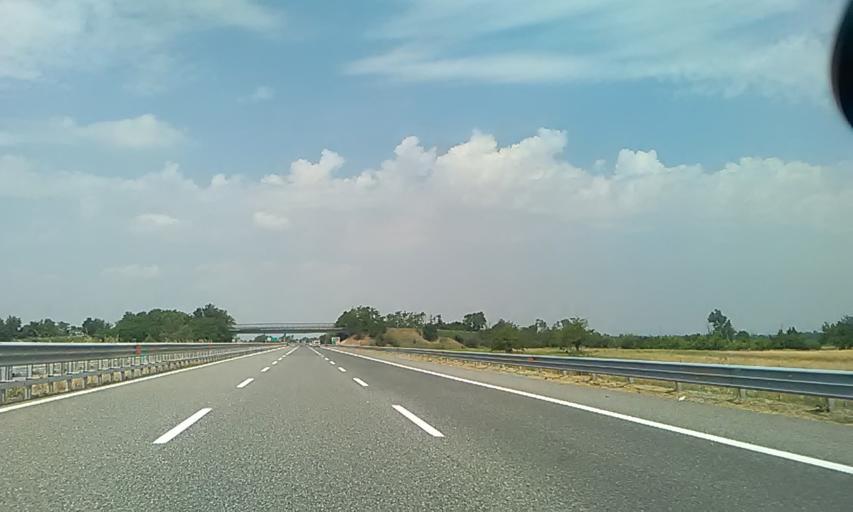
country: IT
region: Piedmont
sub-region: Provincia di Alessandria
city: Castelspina
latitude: 44.8022
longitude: 8.6050
